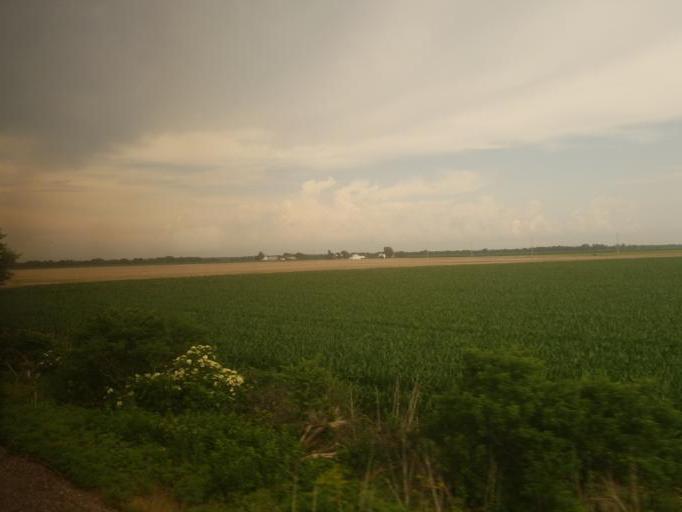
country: US
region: Illinois
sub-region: Bureau County
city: Princeton
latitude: 41.3832
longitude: -89.5312
